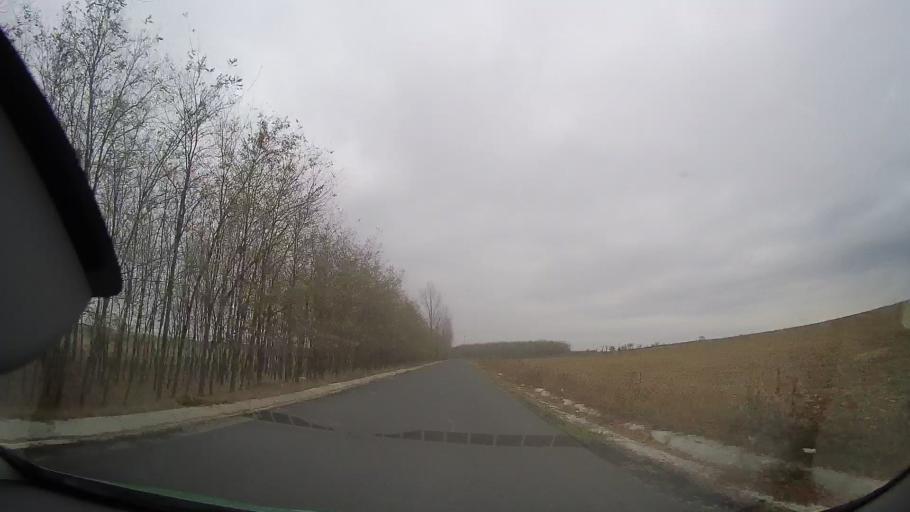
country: RO
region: Braila
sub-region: Comuna Ciocile
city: Ciocile
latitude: 44.7935
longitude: 27.2761
